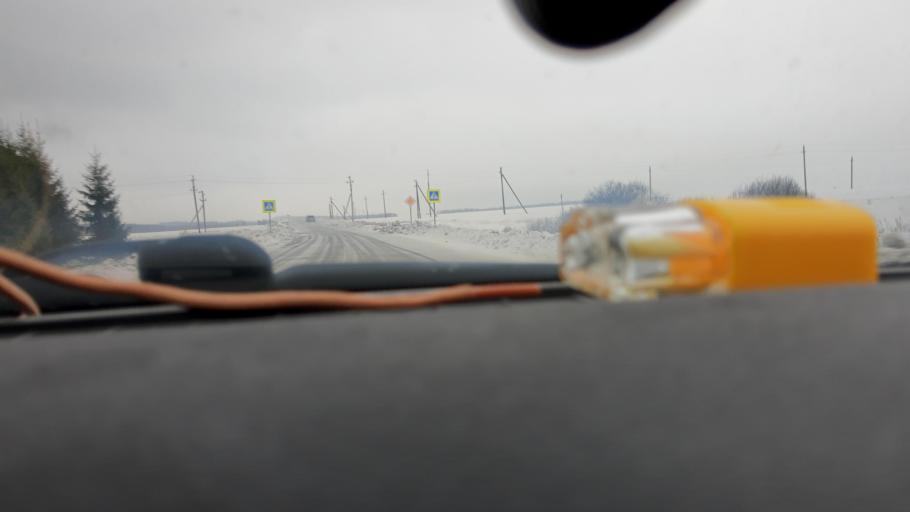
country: RU
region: Bashkortostan
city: Ulukulevo
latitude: 54.6030
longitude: 56.4267
